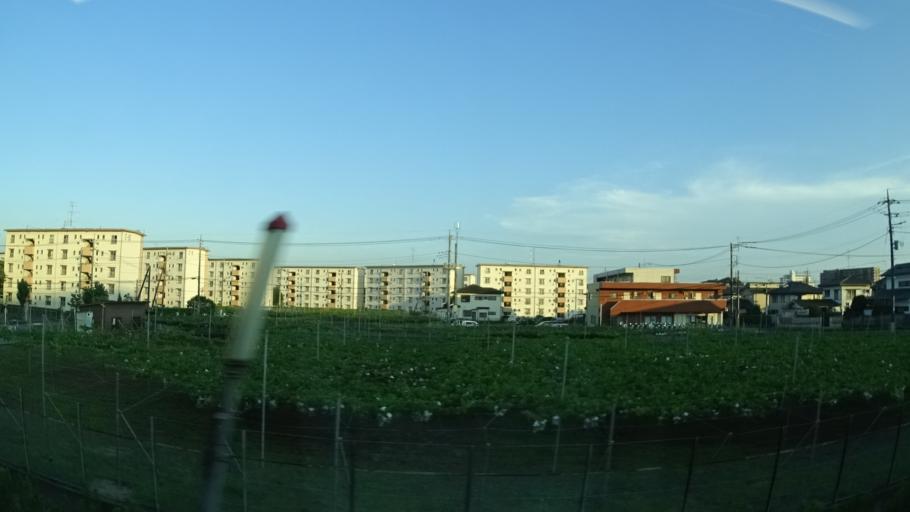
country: JP
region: Ibaraki
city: Toride
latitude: 35.9005
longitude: 140.0728
